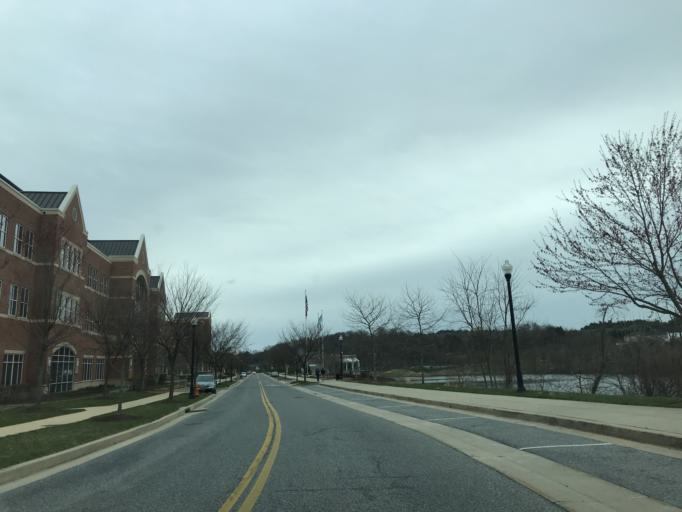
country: US
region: Maryland
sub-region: Baltimore County
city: Pikesville
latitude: 39.3841
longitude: -76.6927
